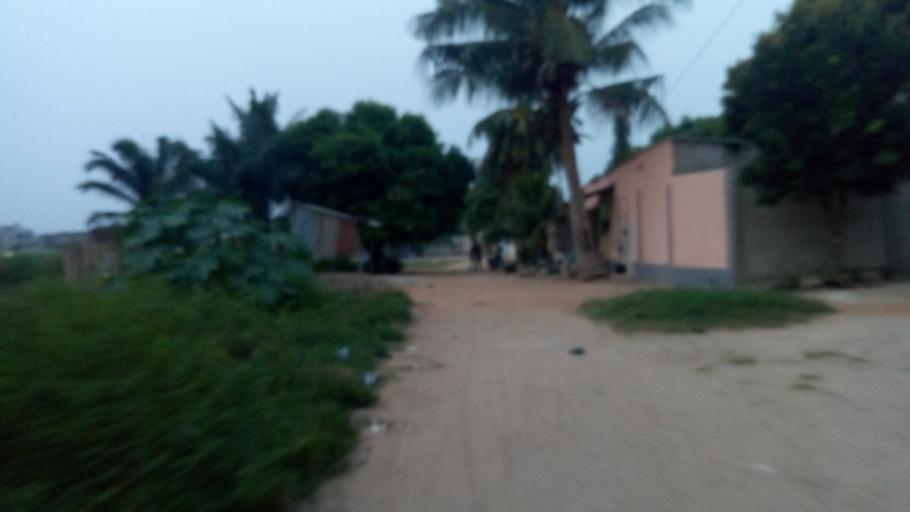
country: TG
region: Maritime
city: Lome
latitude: 6.1757
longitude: 1.1773
